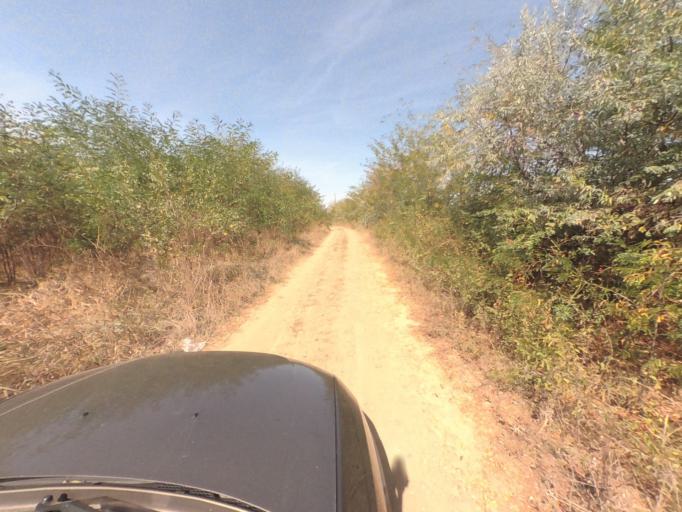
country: RO
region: Vaslui
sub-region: Comuna Costesti
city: Costesti
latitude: 46.5193
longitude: 27.7408
